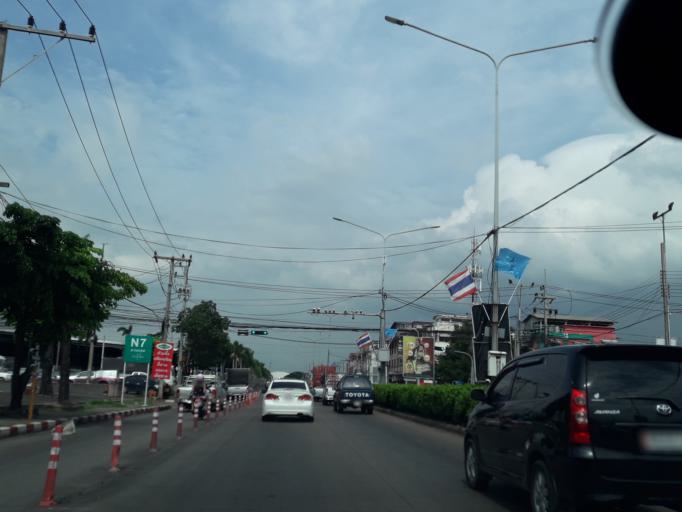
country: TH
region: Pathum Thani
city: Khlong Luang
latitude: 14.0818
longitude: 100.6306
